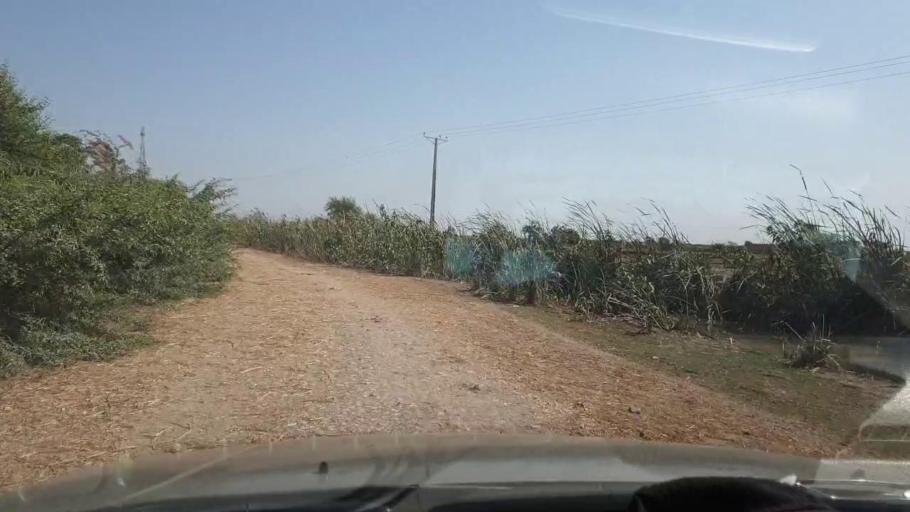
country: PK
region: Sindh
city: Daro Mehar
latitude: 24.9695
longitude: 68.1178
